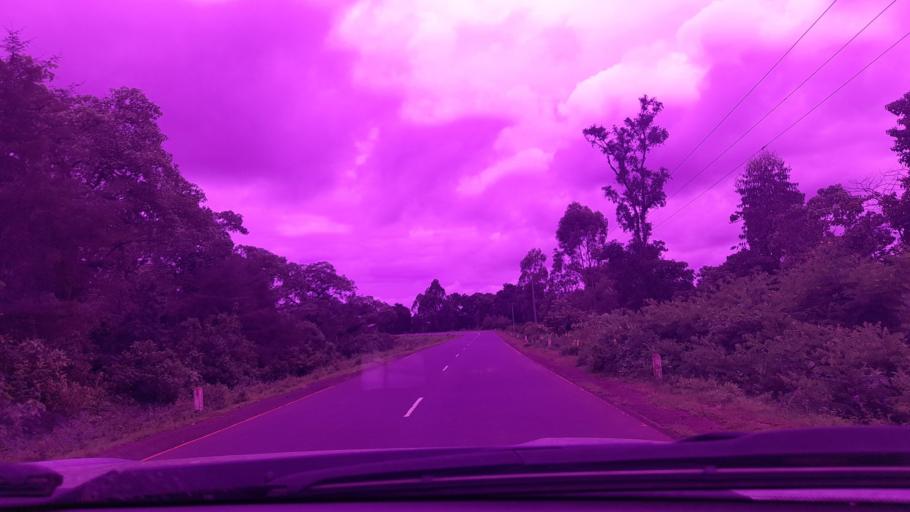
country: ET
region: Southern Nations, Nationalities, and People's Region
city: Bonga
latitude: 7.2825
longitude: 35.9580
